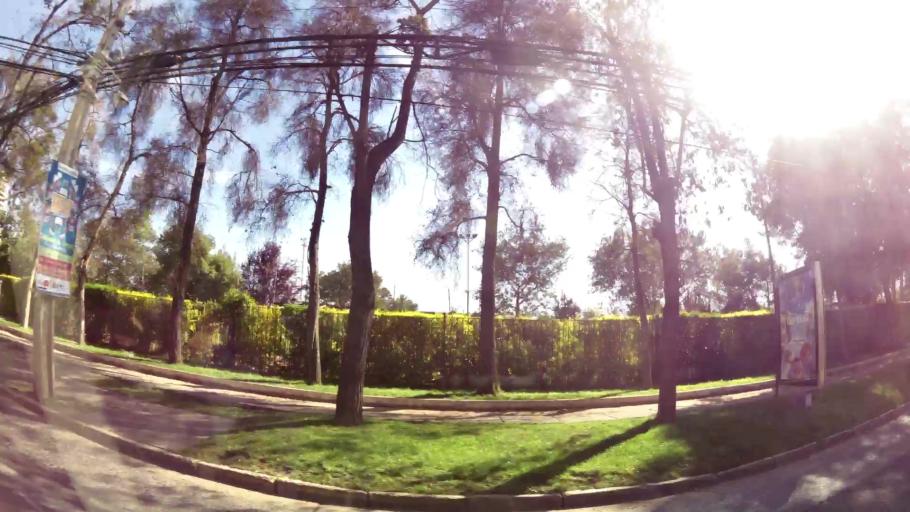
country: CL
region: Santiago Metropolitan
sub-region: Provincia de Santiago
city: Villa Presidente Frei, Nunoa, Santiago, Chile
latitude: -33.4380
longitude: -70.5709
